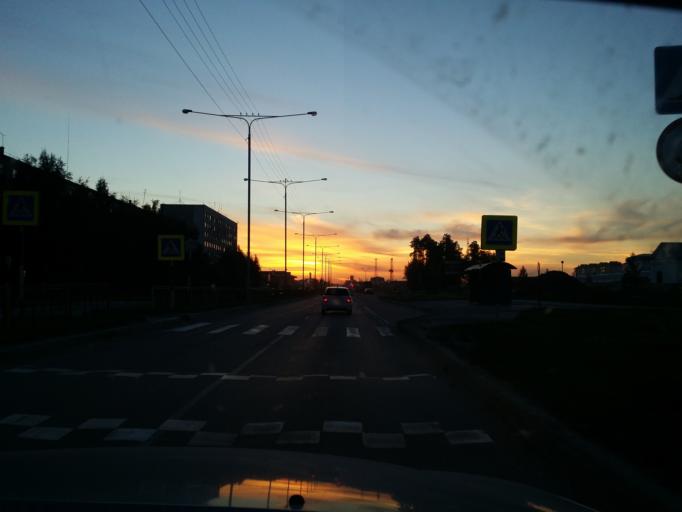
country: RU
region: Khanty-Mansiyskiy Avtonomnyy Okrug
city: Nizhnevartovsk
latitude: 60.9484
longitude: 76.5647
